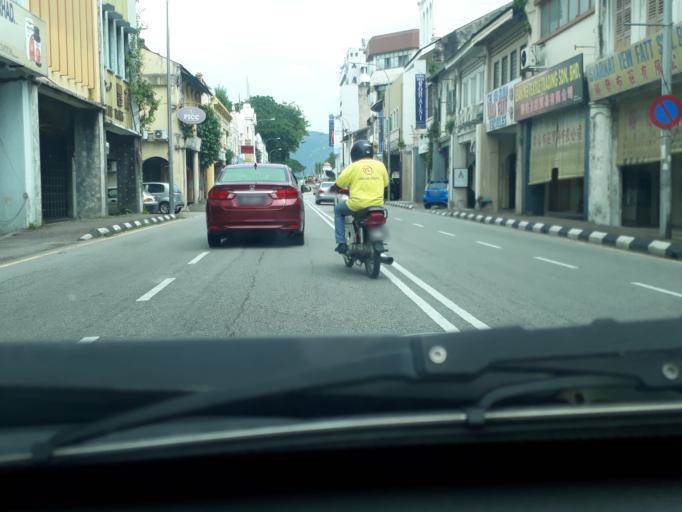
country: MY
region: Perak
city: Ipoh
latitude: 4.5949
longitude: 101.0783
